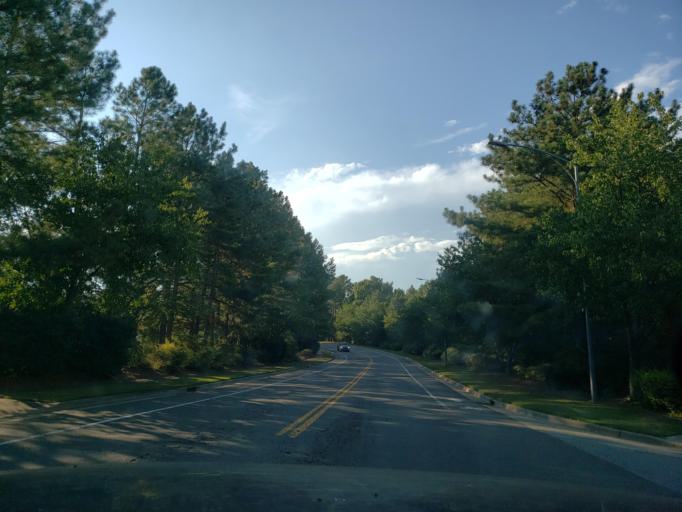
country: US
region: North Carolina
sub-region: Durham County
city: Durham
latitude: 35.9372
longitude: -78.9239
